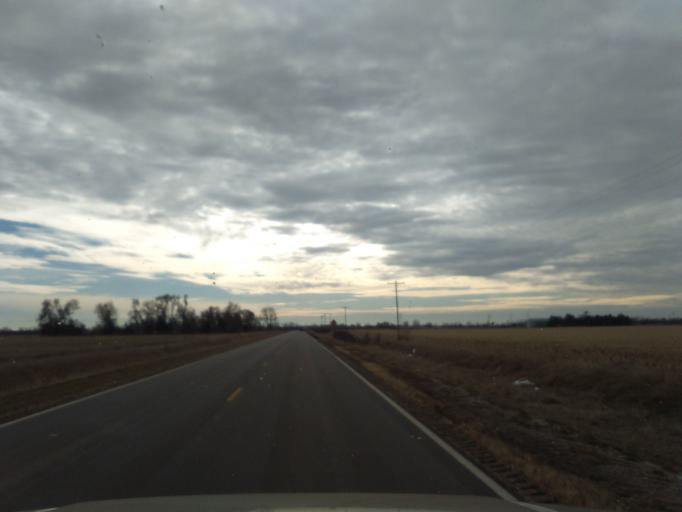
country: US
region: Nebraska
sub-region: Buffalo County
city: Shelton
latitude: 40.7030
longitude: -98.7406
